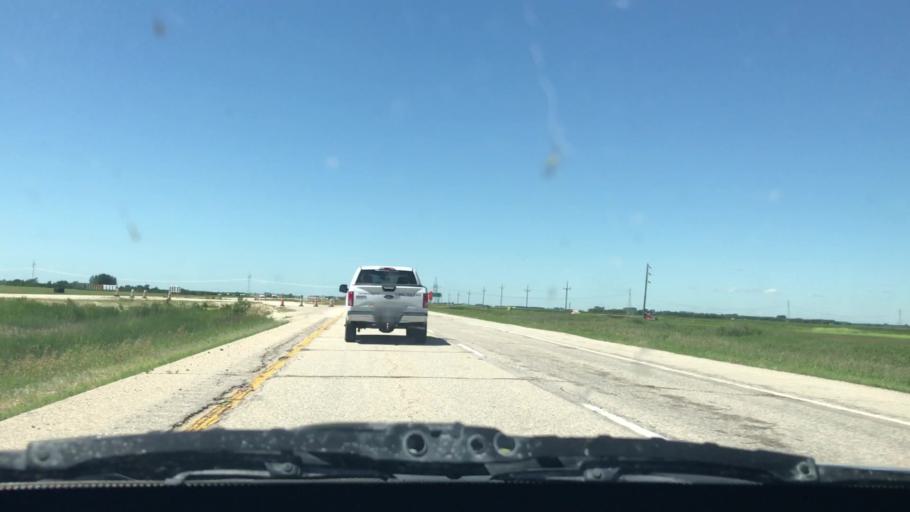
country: CA
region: Manitoba
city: Steinbach
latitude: 49.7062
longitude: -96.6584
